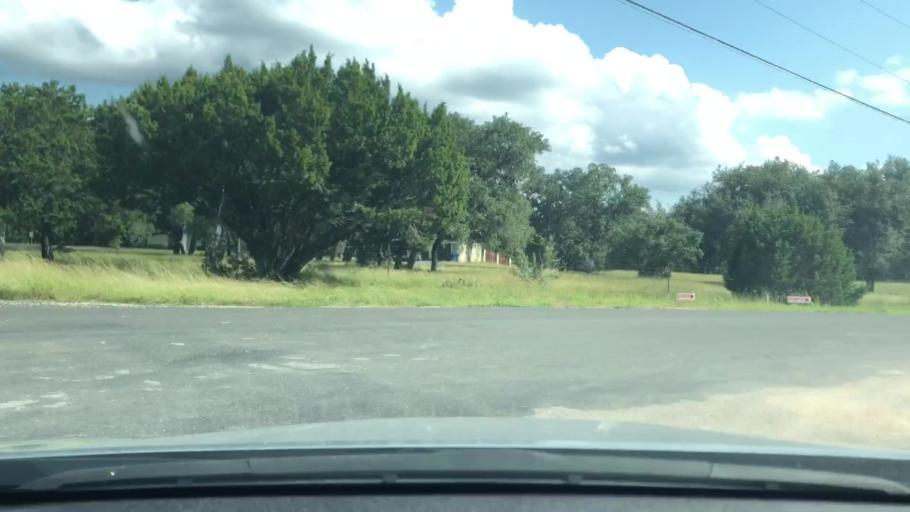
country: US
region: Texas
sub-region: Bexar County
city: Fair Oaks Ranch
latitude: 29.7705
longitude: -98.6254
